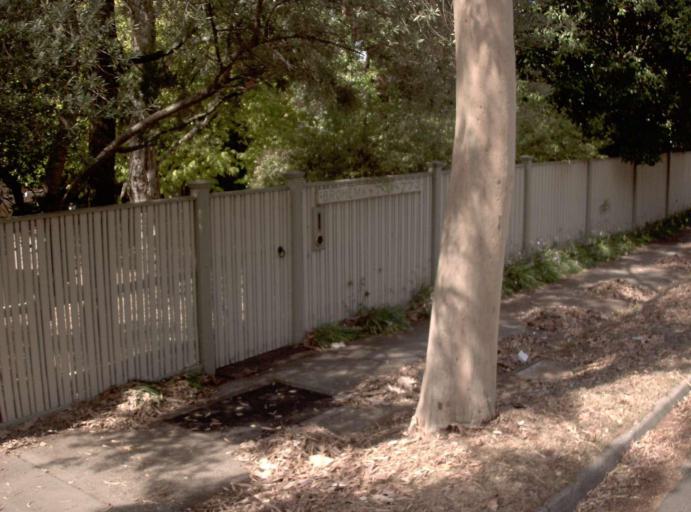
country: AU
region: Victoria
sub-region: Whitehorse
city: Vermont South
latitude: -37.8900
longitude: 145.1748
